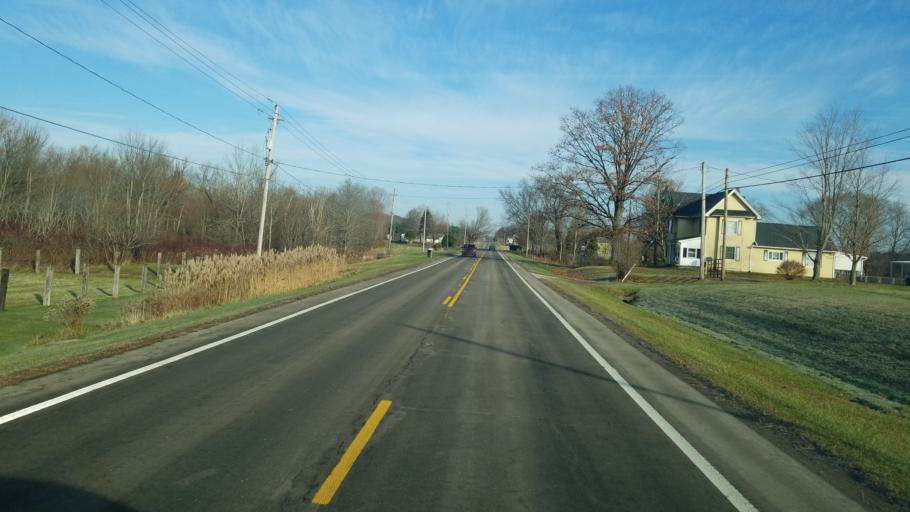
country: US
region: Ohio
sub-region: Ashtabula County
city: North Kingsville
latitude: 41.8308
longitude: -80.6643
